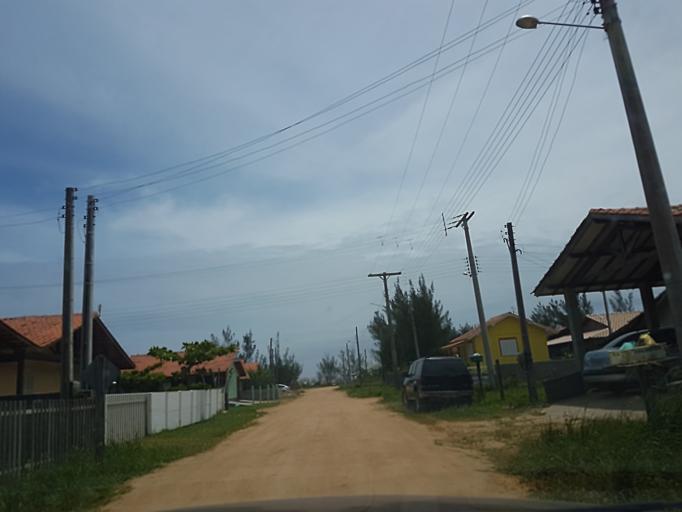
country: BR
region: Santa Catarina
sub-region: Jaguaruna
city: Jaguaruna
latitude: -28.6624
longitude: -48.9616
